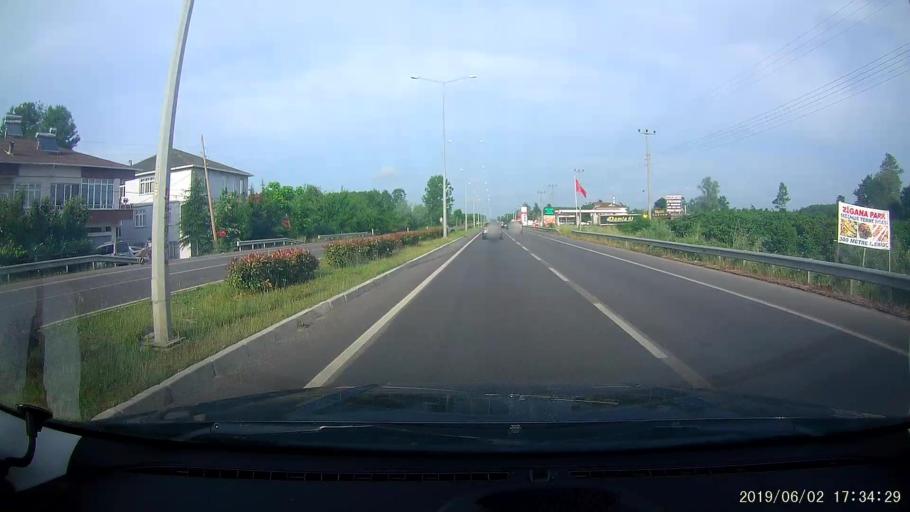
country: TR
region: Samsun
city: Terme
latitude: 41.2202
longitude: 36.8697
